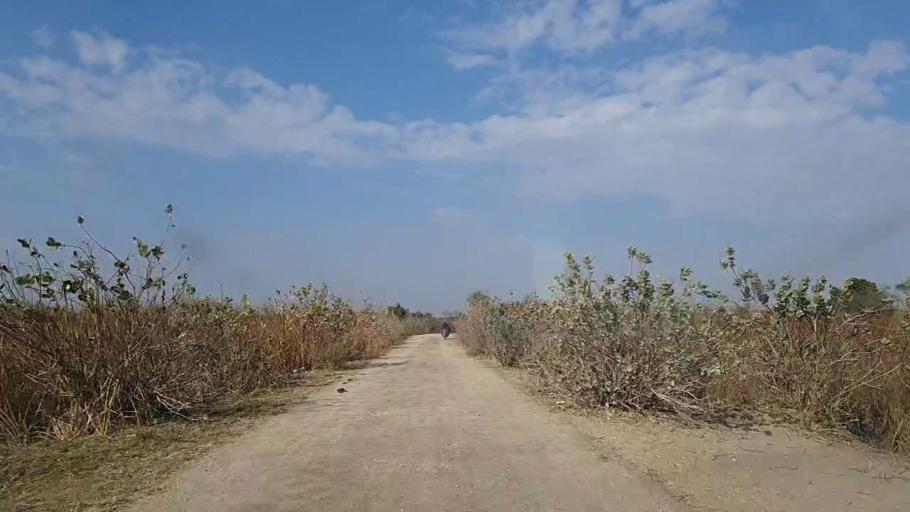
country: PK
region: Sindh
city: Sanghar
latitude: 26.2668
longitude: 69.0118
